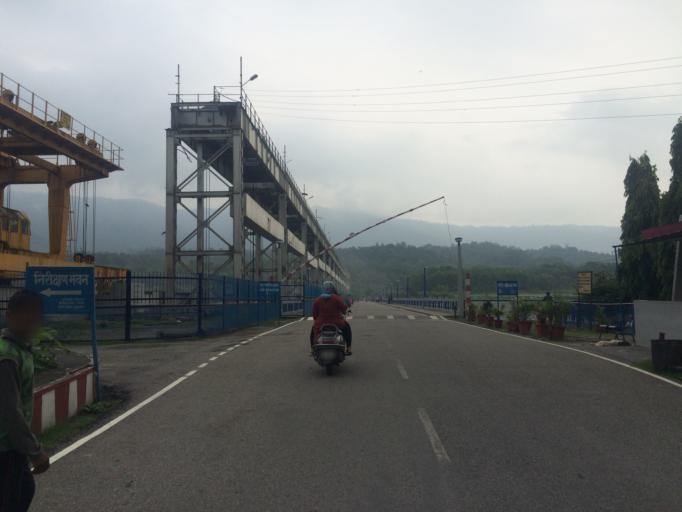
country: IN
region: Uttarakhand
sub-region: Dehradun
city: Birbhaddar
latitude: 30.0749
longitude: 78.2868
